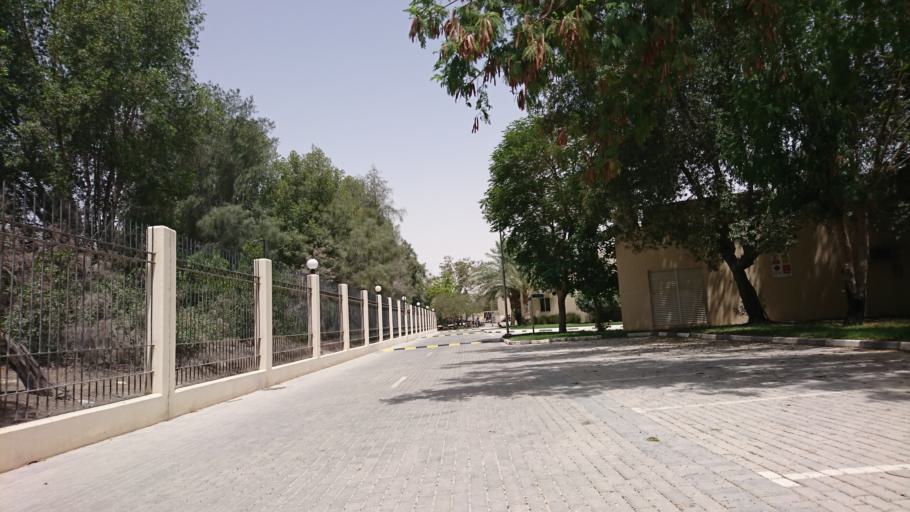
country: QA
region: Baladiyat ad Dawhah
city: Doha
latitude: 25.3841
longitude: 51.5133
